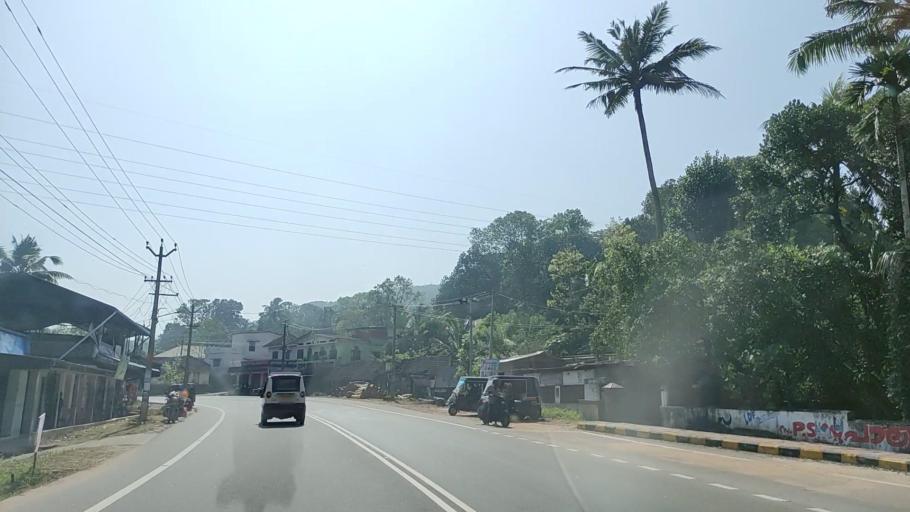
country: IN
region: Kerala
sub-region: Kollam
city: Punalur
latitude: 8.9334
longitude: 76.9621
